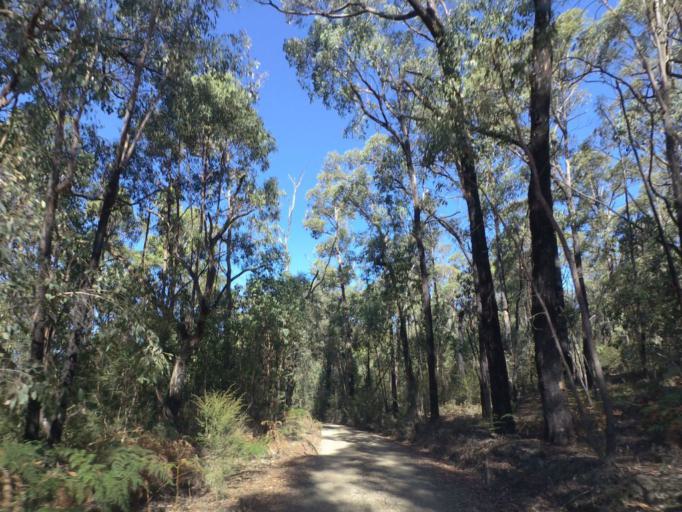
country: AU
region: Victoria
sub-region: Murrindindi
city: Kinglake West
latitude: -37.4629
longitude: 145.3808
